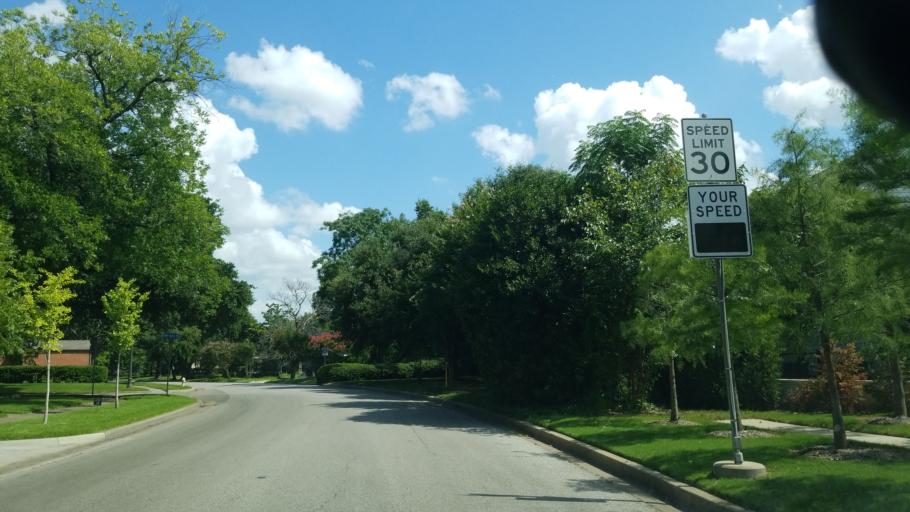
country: US
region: Texas
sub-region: Dallas County
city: Highland Park
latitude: 32.8291
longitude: -96.8191
